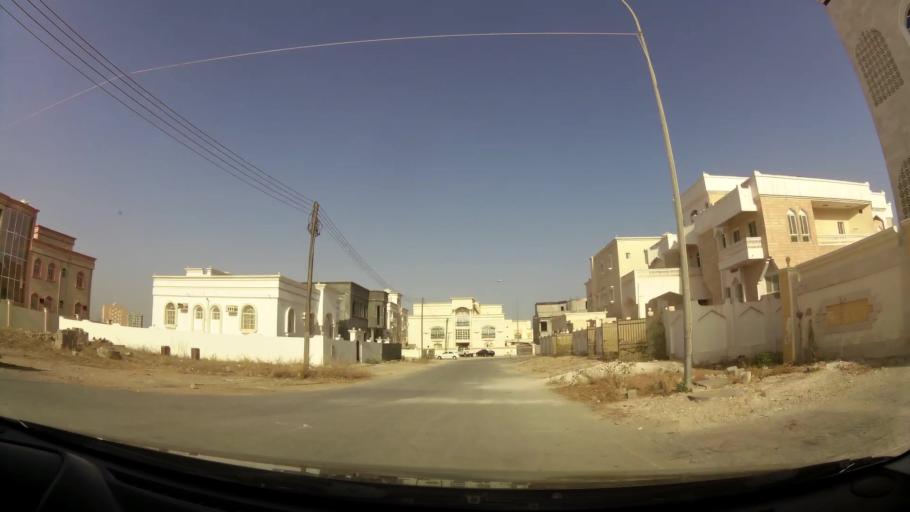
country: OM
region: Zufar
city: Salalah
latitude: 17.0234
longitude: 54.0256
